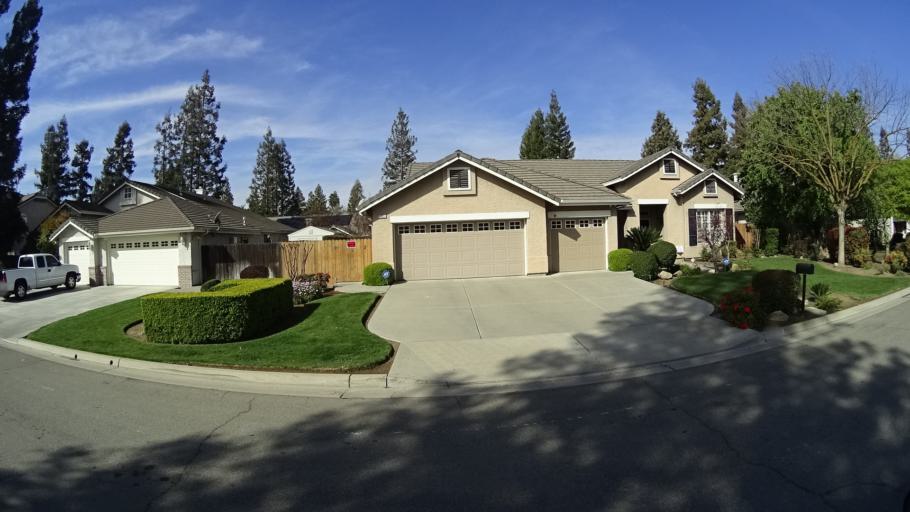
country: US
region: California
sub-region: Fresno County
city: West Park
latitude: 36.8417
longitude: -119.8765
